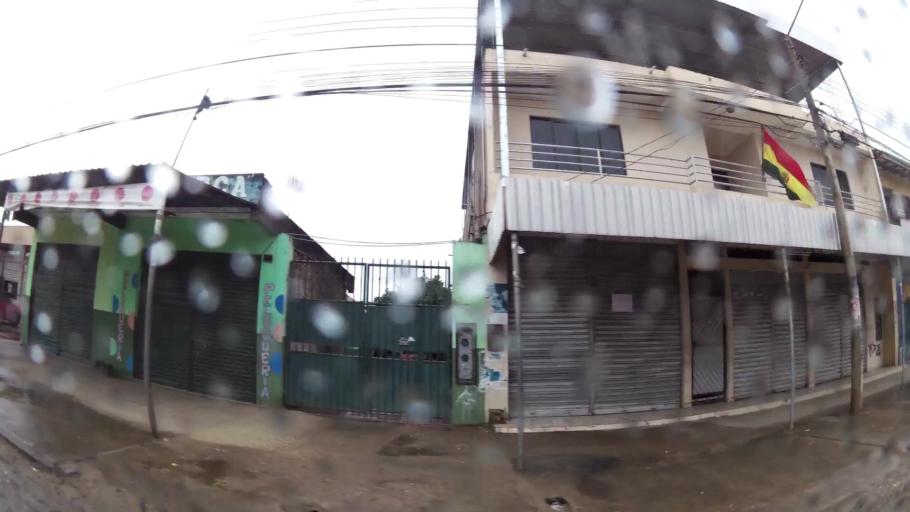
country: BO
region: Santa Cruz
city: Santa Cruz de la Sierra
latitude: -17.8064
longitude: -63.1282
